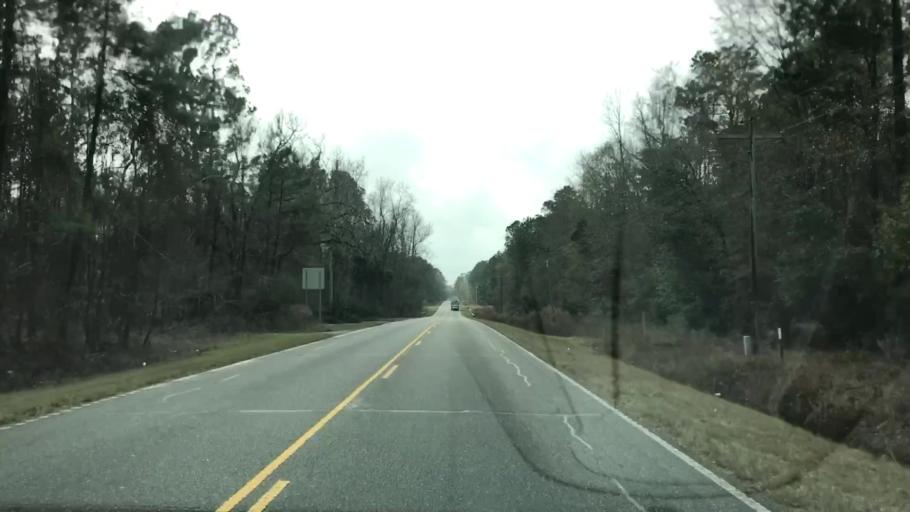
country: US
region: South Carolina
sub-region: Georgetown County
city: Murrells Inlet
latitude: 33.6478
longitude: -79.1714
